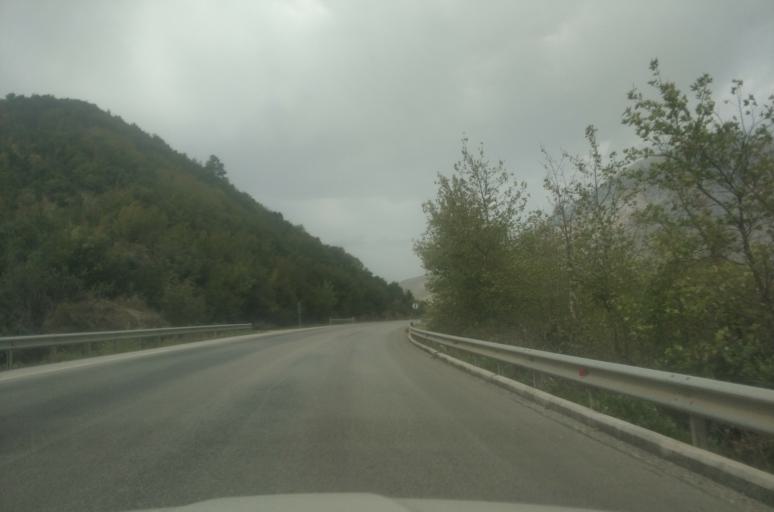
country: AL
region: Gjirokaster
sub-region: Rrethi i Tepelenes
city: Tepelene
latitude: 40.2604
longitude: 20.0526
